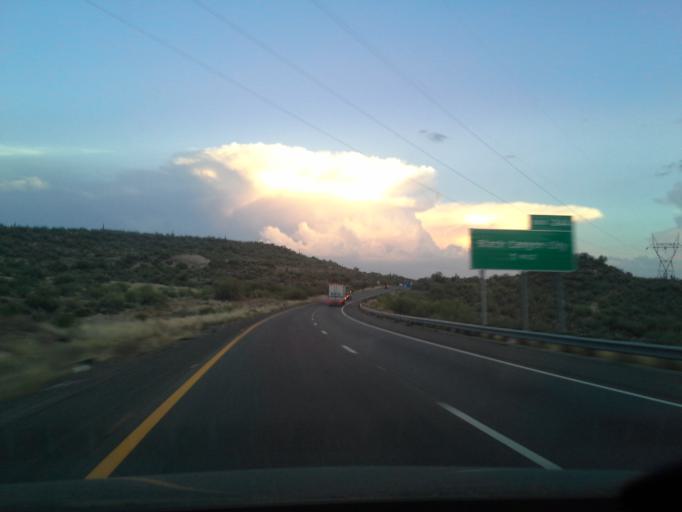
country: US
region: Arizona
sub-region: Yavapai County
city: Black Canyon City
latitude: 34.1035
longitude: -112.1430
